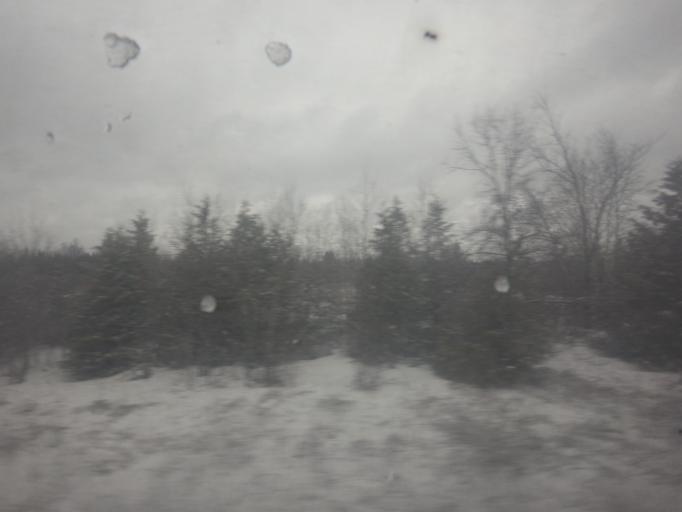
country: CA
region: Ontario
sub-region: Lanark County
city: Smiths Falls
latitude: 44.9559
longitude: -76.0069
